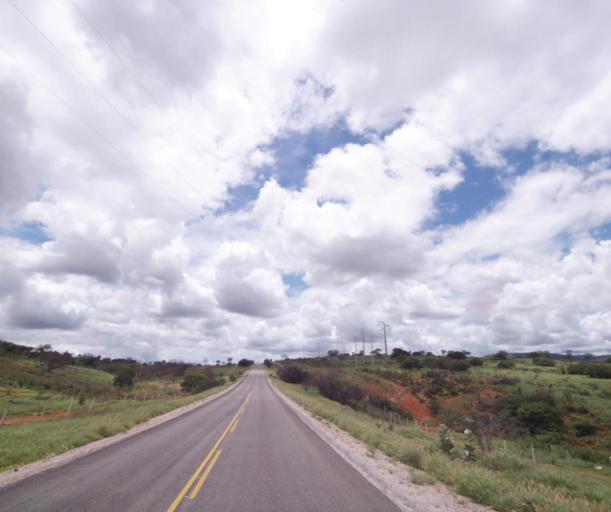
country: BR
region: Bahia
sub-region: Brumado
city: Brumado
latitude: -14.1520
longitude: -41.5100
